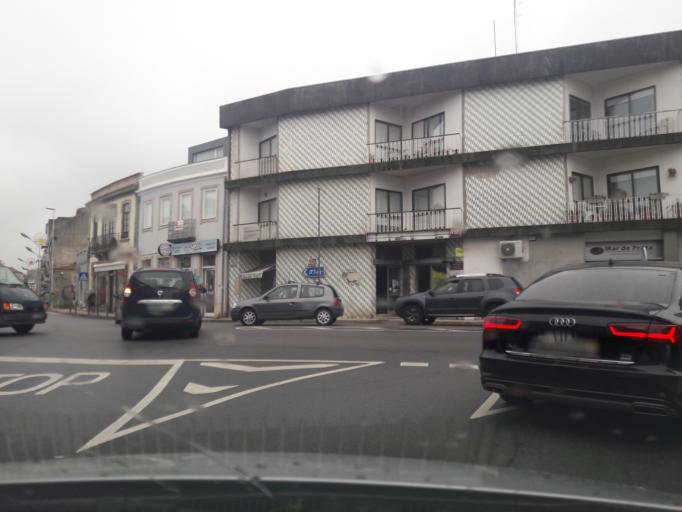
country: PT
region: Porto
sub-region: Vila do Conde
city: Vila do Conde
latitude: 41.3531
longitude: -8.7407
